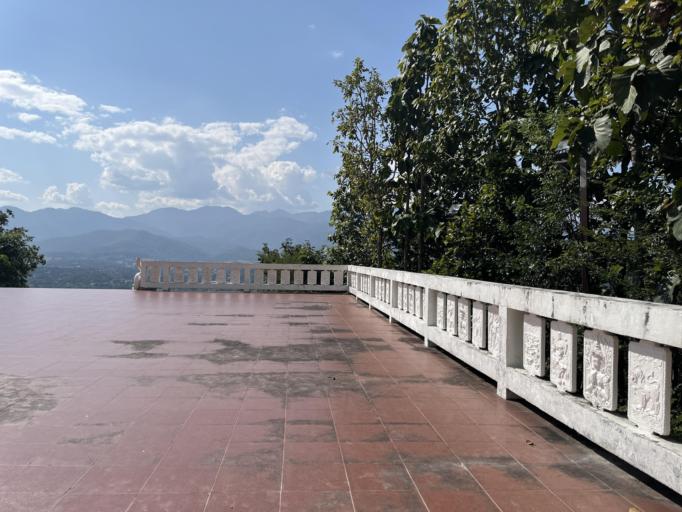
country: TH
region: Mae Hong Son
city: Mae Hi
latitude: 19.3503
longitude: 98.4561
